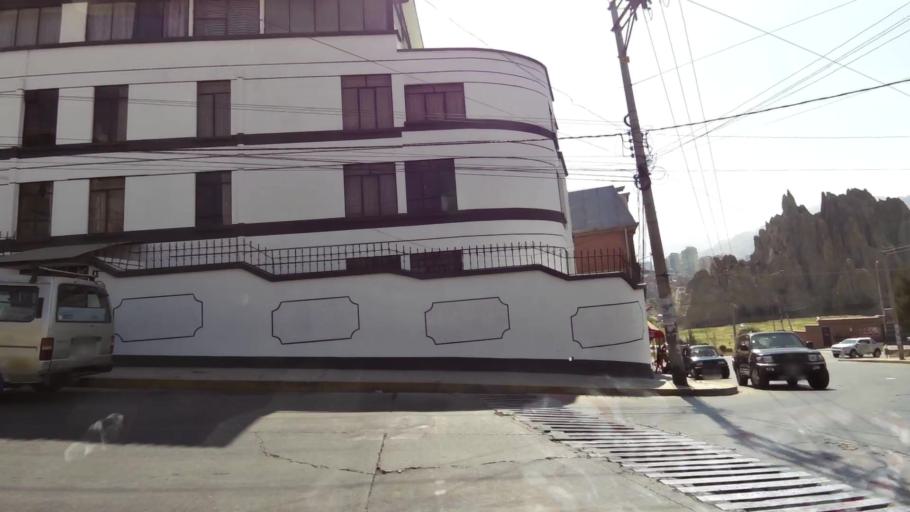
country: BO
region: La Paz
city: La Paz
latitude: -16.5237
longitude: -68.1222
